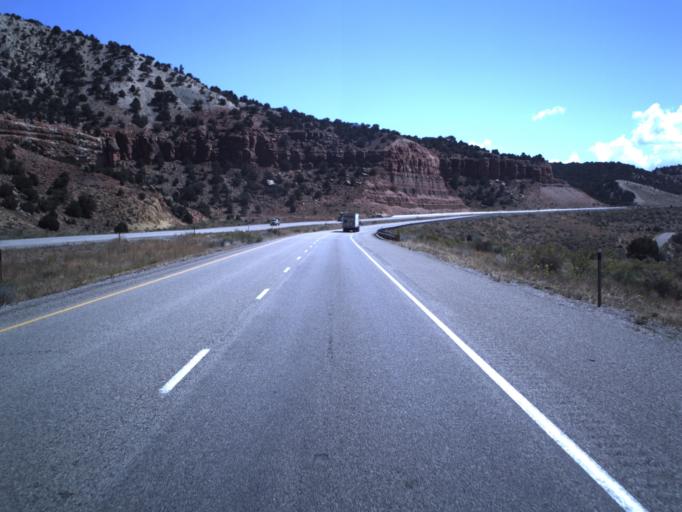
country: US
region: Utah
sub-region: Sevier County
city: Salina
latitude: 38.9327
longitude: -111.7945
